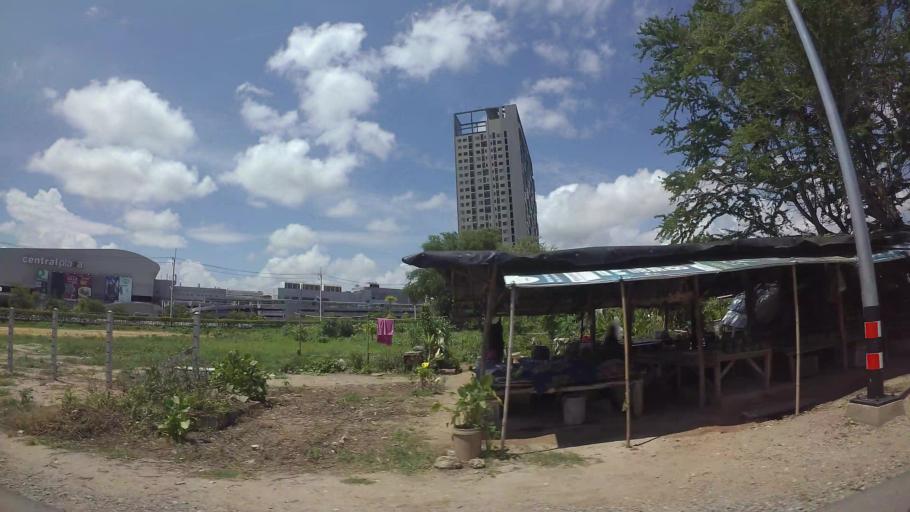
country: TH
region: Rayong
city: Rayong
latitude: 12.6936
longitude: 101.2675
